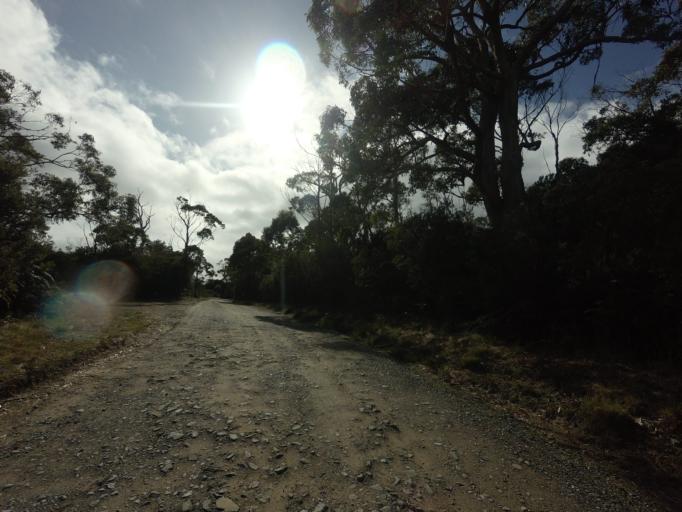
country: AU
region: Tasmania
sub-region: Huon Valley
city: Geeveston
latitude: -43.5804
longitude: 146.8987
